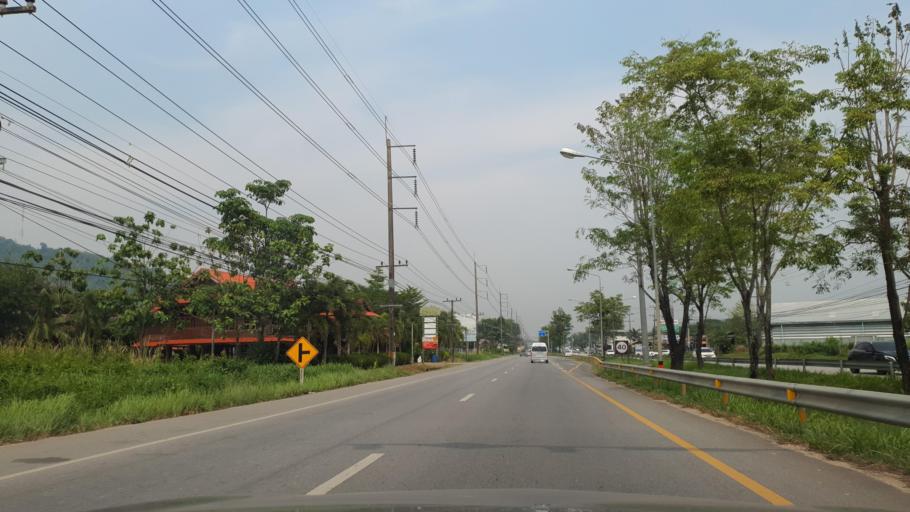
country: TH
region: Rayong
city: Rayong
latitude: 12.6413
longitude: 101.4067
